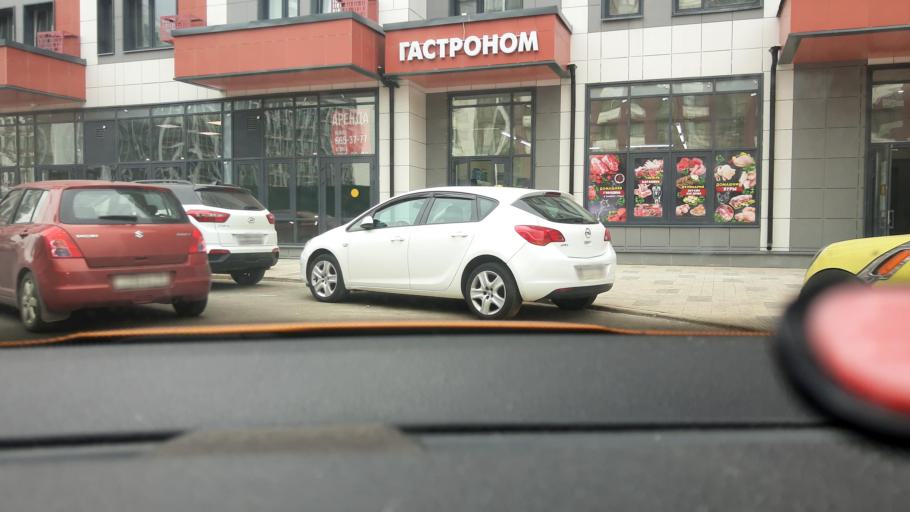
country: RU
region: Moscow
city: Zapadnoye Degunino
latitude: 55.8777
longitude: 37.5384
